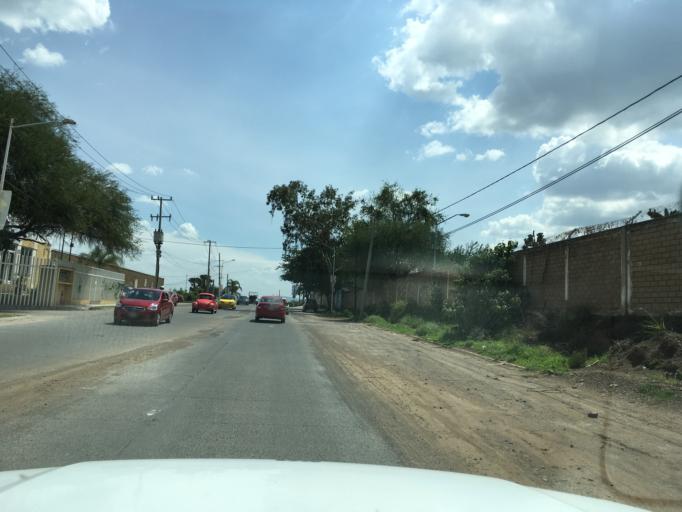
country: MX
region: Jalisco
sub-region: Tlajomulco de Zuniga
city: Altus Bosques
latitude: 20.5837
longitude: -103.3600
